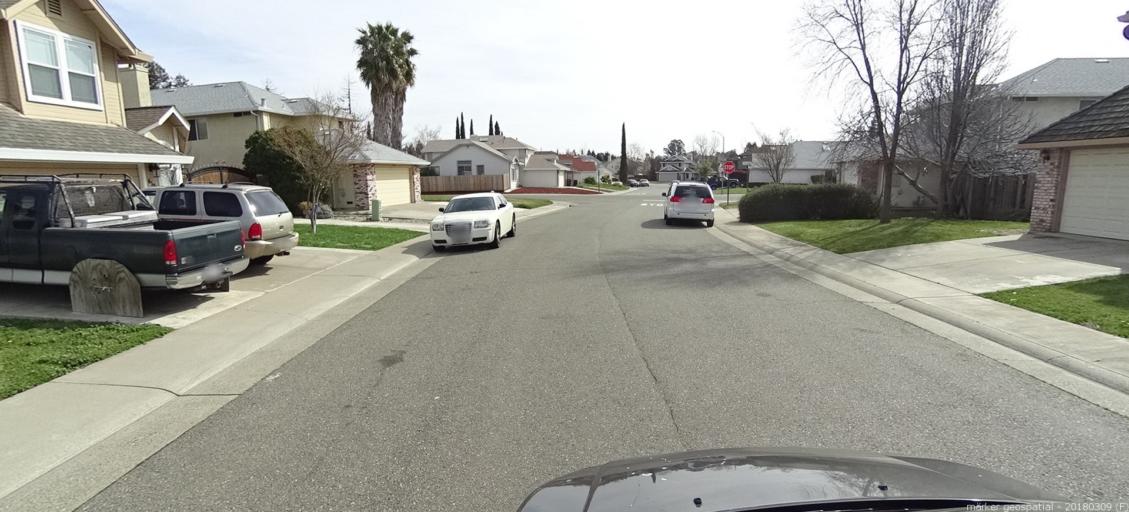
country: US
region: California
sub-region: Sacramento County
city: Florin
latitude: 38.4592
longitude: -121.3956
